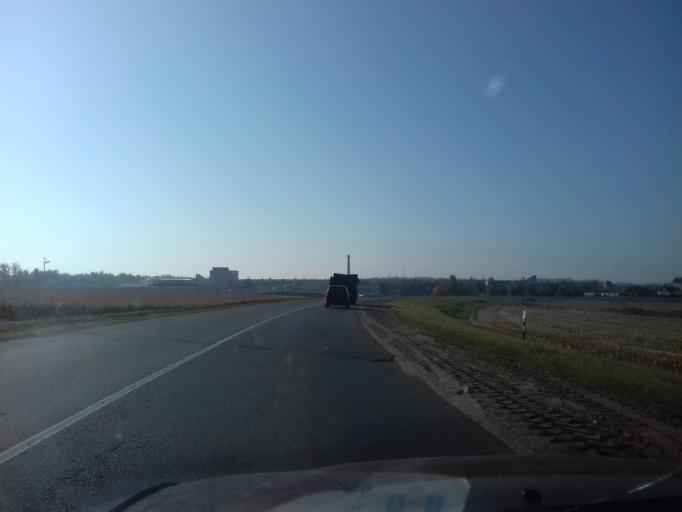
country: BY
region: Minsk
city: Hatava
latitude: 53.7820
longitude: 27.6542
